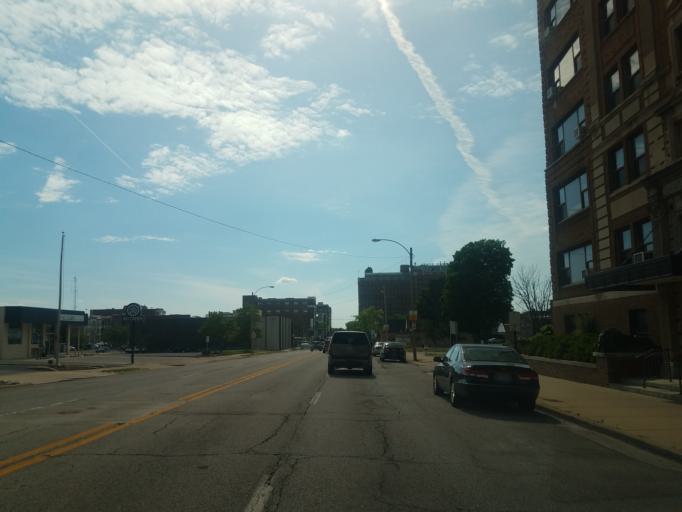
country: US
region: Illinois
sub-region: McLean County
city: Bloomington
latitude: 40.4797
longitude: -88.9886
